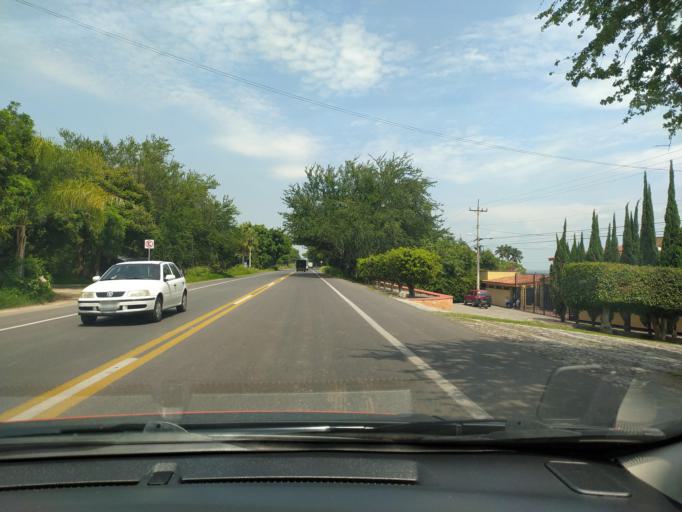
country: MX
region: Jalisco
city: San Juan Cosala
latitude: 20.2913
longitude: -103.3628
